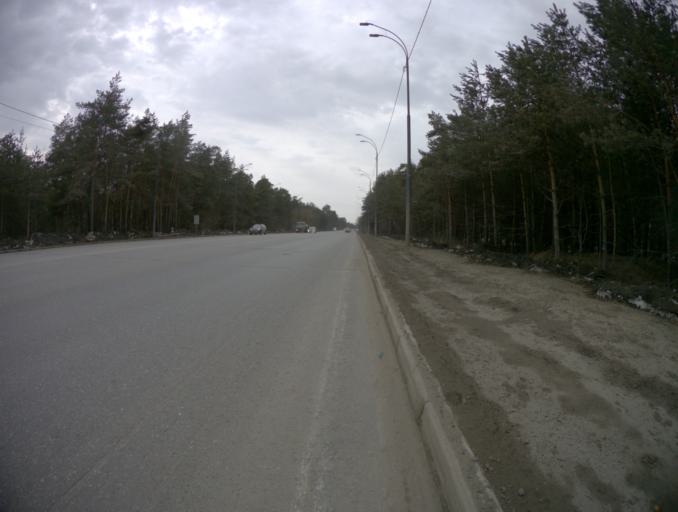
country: RU
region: Vladimir
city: Kommunar
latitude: 56.0987
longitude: 40.4433
